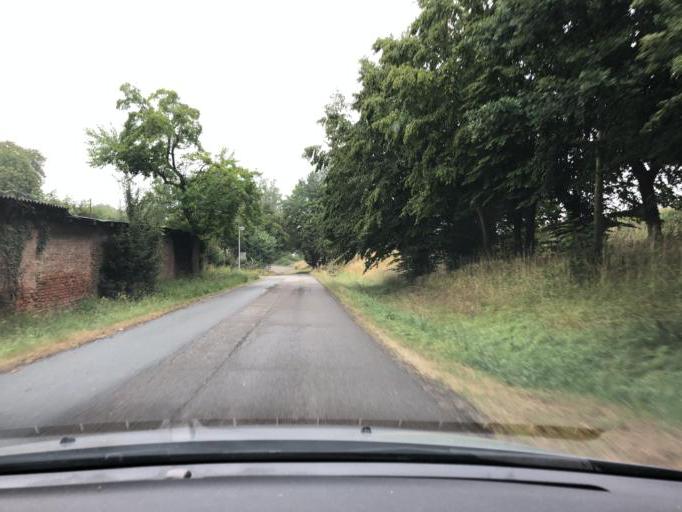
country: DE
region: Thuringia
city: Langenleuba-Niederhain
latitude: 51.0118
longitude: 12.6129
